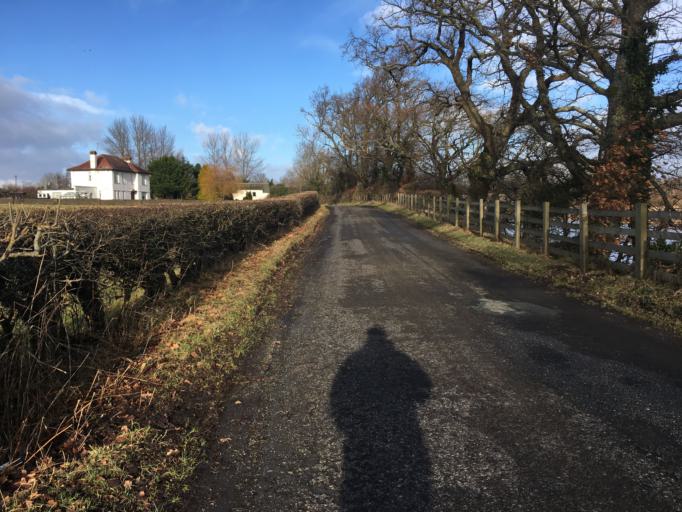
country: GB
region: Scotland
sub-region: Stirling
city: Bridge of Allan
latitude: 56.1358
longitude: -3.9811
